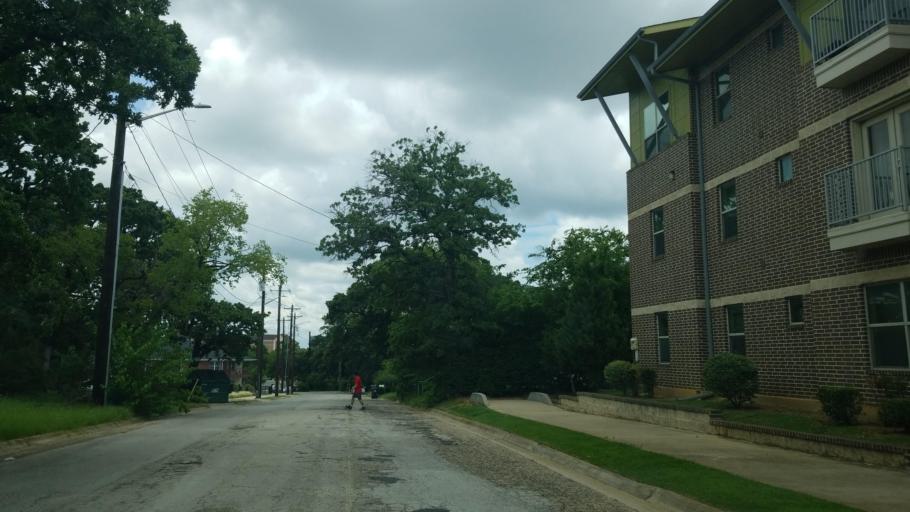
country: US
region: Texas
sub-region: Denton County
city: Denton
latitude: 33.2021
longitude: -97.1458
